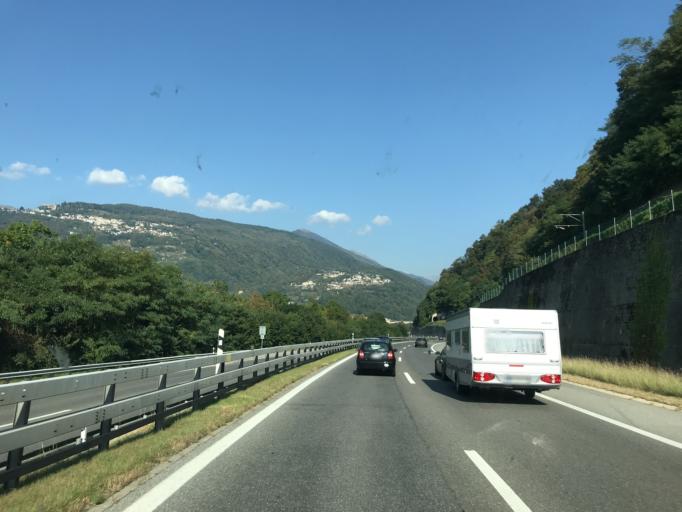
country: CH
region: Ticino
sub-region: Lugano District
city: Agno
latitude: 45.9989
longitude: 8.9154
